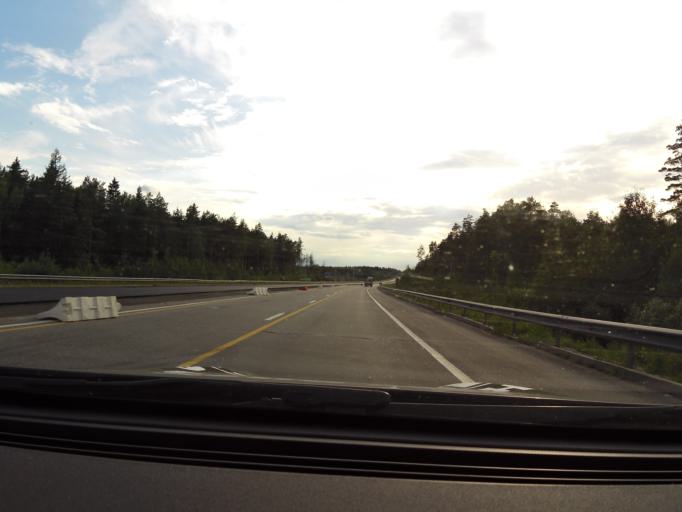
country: RU
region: Vladimir
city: Orgtrud
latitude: 56.1026
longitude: 40.7690
